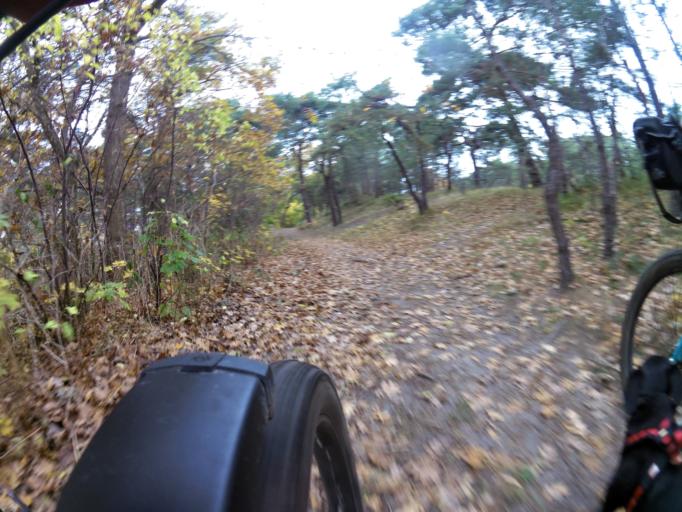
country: PL
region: Pomeranian Voivodeship
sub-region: Powiat pucki
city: Jastarnia
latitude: 54.6970
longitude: 18.6884
